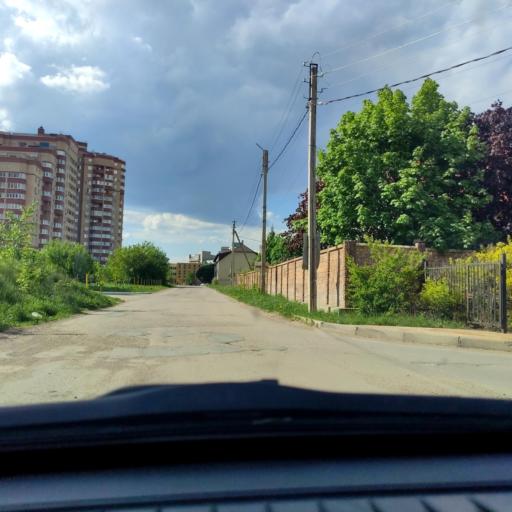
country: RU
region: Samara
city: Tol'yatti
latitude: 53.5383
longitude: 49.3646
